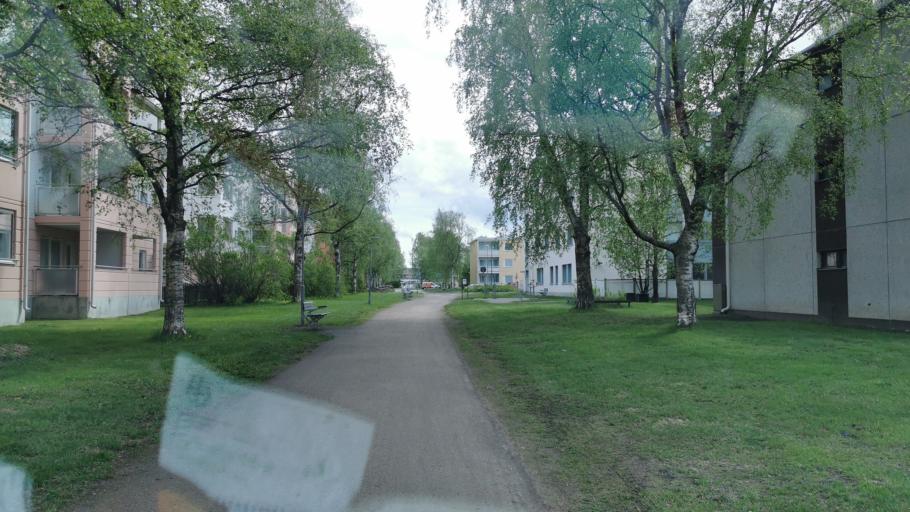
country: FI
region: Northern Ostrobothnia
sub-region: Oulu
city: Oulu
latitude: 65.0040
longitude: 25.4587
